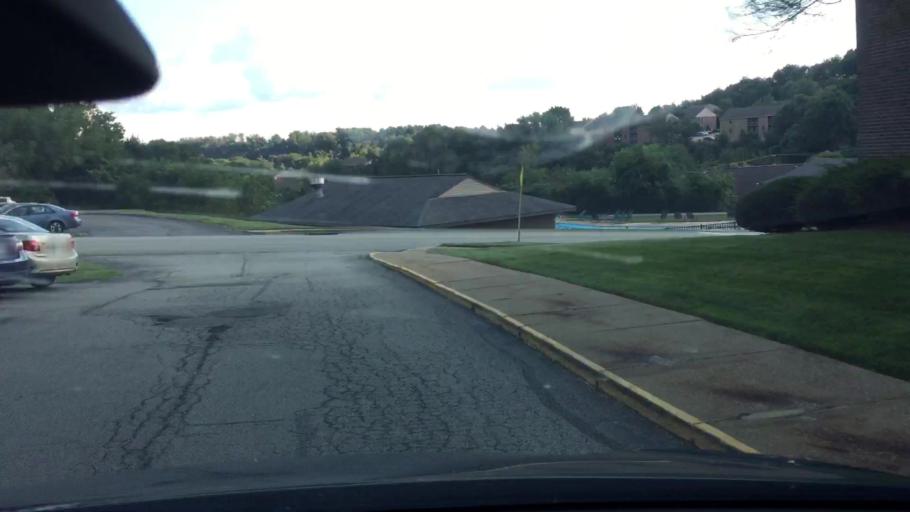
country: US
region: Pennsylvania
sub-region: Allegheny County
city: Monroeville
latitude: 40.4358
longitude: -79.7630
